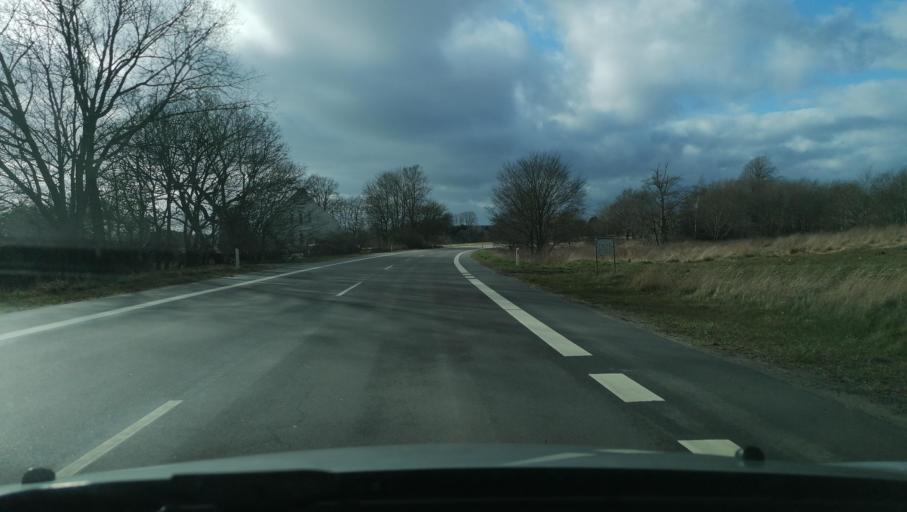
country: DK
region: Zealand
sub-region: Odsherred Kommune
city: Horve
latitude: 55.7647
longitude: 11.4330
